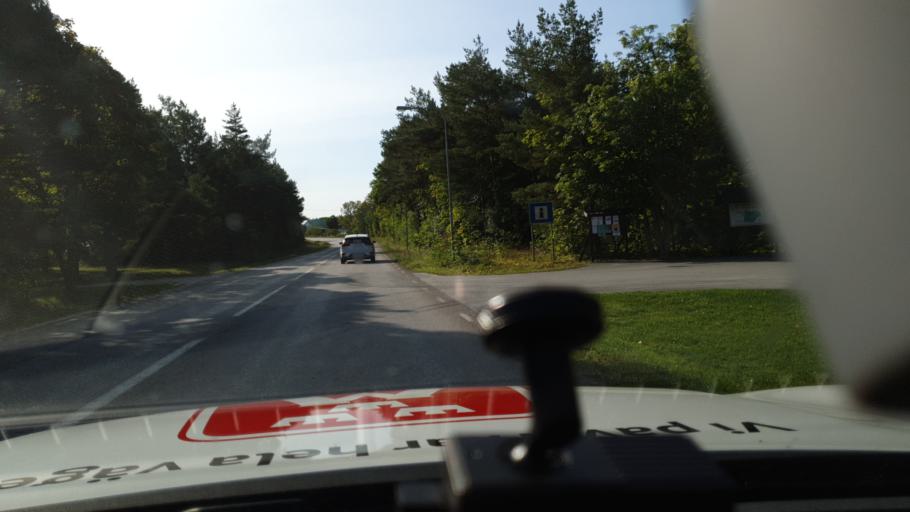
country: SE
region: Gotland
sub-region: Gotland
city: Klintehamn
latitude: 57.3355
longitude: 18.1909
